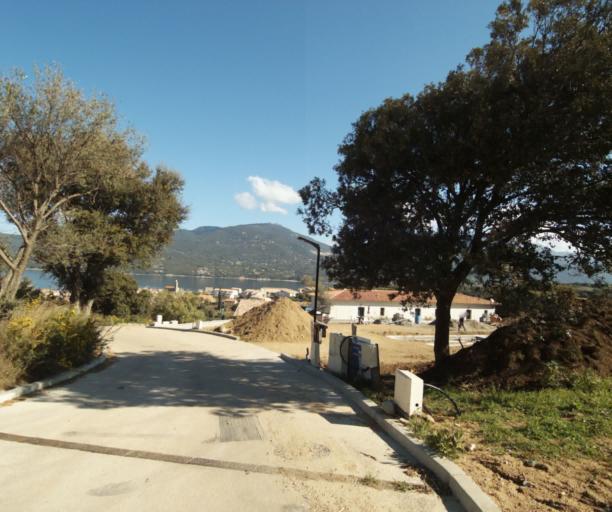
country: FR
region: Corsica
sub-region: Departement de la Corse-du-Sud
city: Propriano
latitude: 41.6687
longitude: 8.9070
